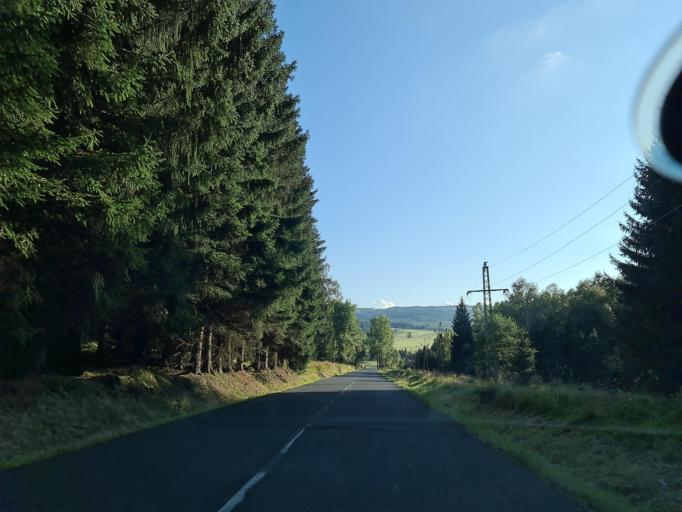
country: DE
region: Saxony
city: Deutschneudorf
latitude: 50.6055
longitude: 13.4692
